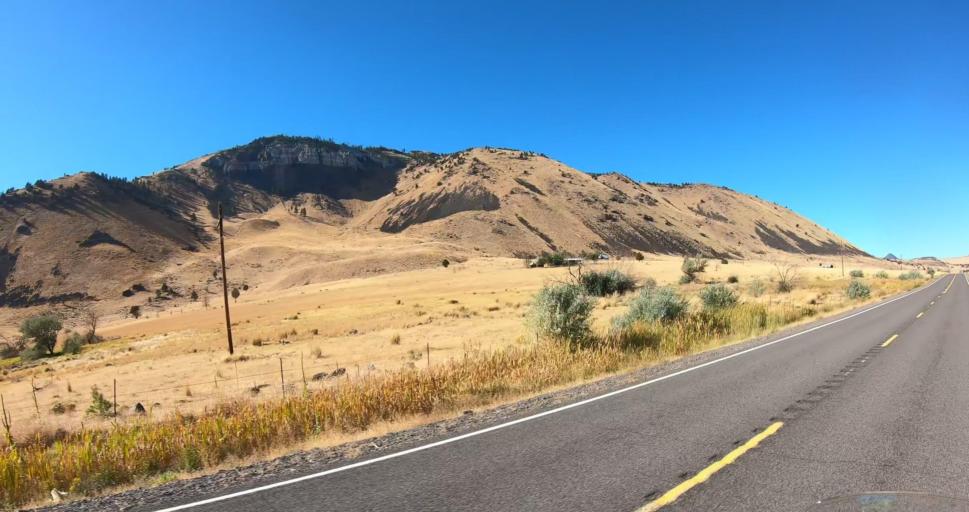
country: US
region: Oregon
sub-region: Lake County
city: Lakeview
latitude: 42.9813
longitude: -120.7770
